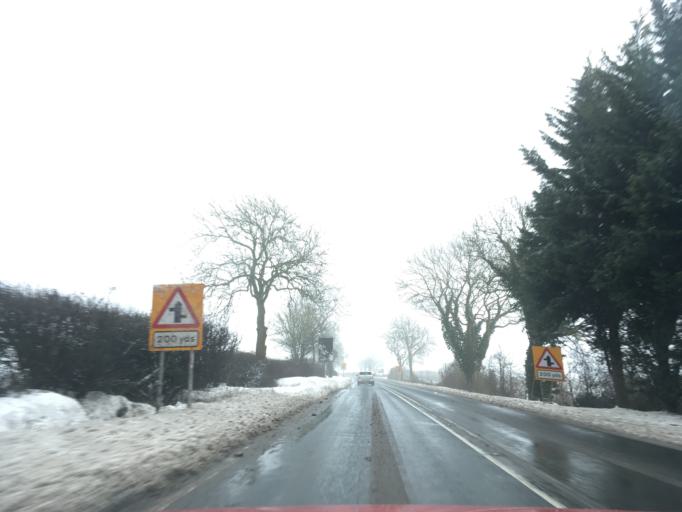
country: GB
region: England
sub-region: Warwickshire
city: Bidford-on-avon
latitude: 52.2029
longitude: -1.7946
